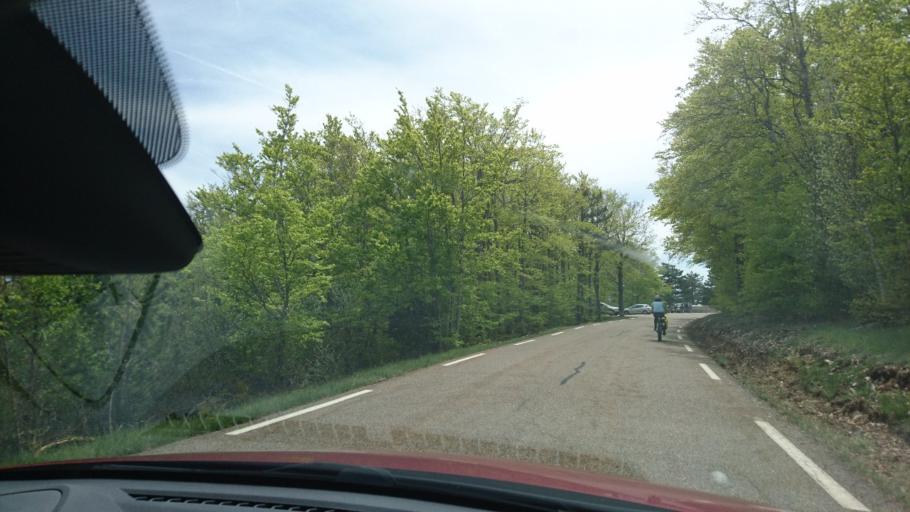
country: FR
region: Provence-Alpes-Cote d'Azur
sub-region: Departement du Vaucluse
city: Sault
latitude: 44.1422
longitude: 5.3451
